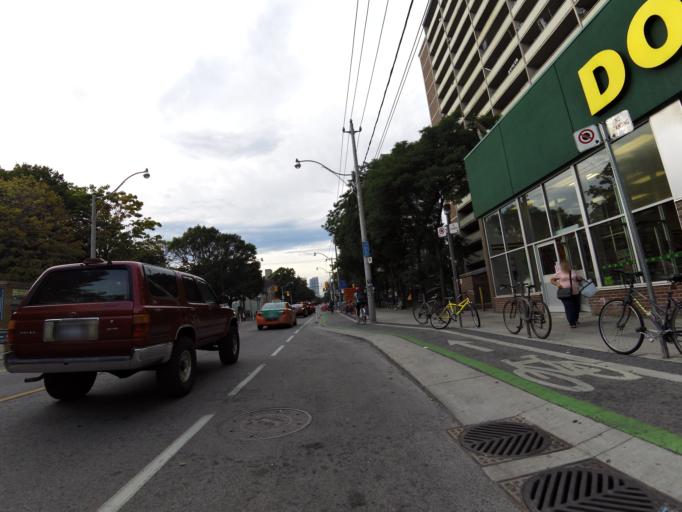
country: CA
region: Ontario
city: Toronto
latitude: 43.6555
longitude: -79.3697
